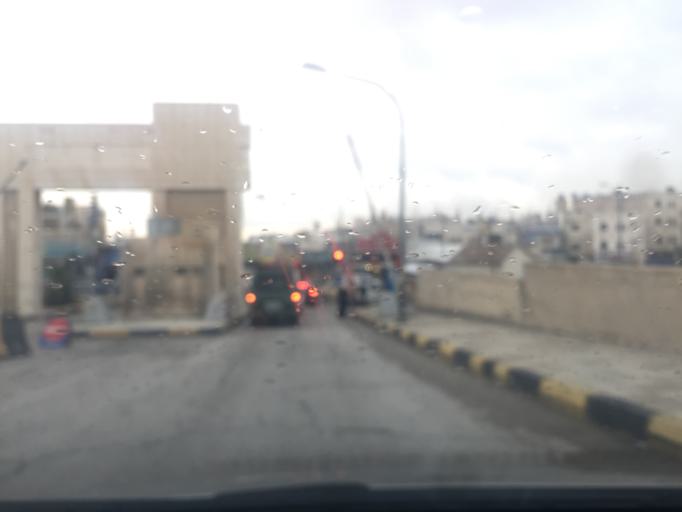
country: JO
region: Zarqa
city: Russeifa
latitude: 32.0308
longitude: 36.0462
